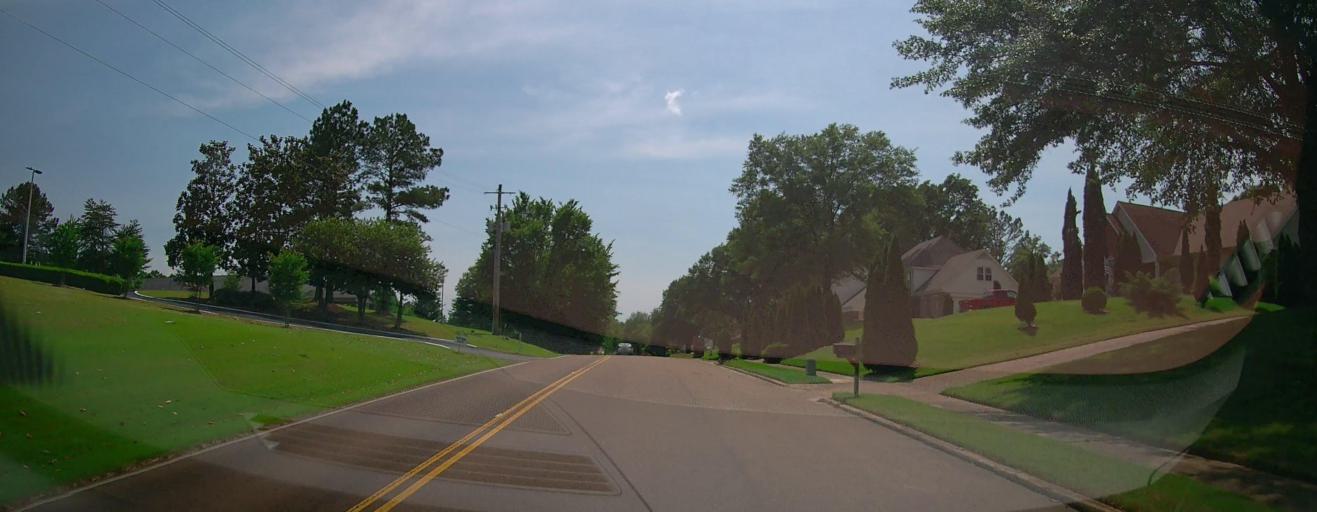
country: US
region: Mississippi
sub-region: De Soto County
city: Olive Branch
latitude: 35.0169
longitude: -89.8261
